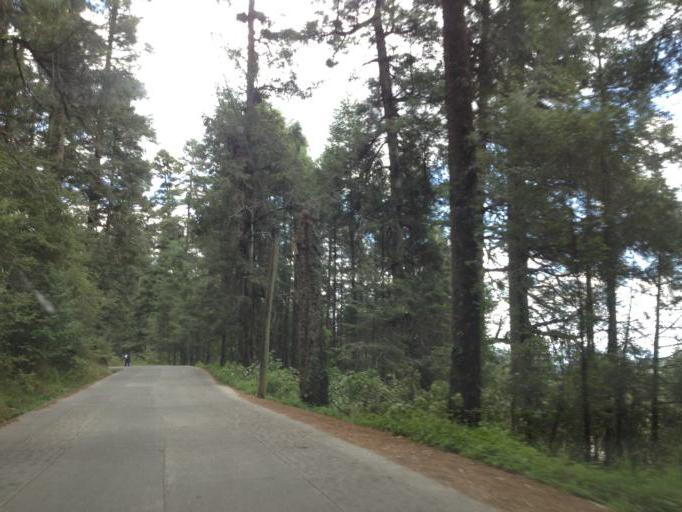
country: MX
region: Hidalgo
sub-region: Pachuca de Soto
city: San Miguel Cerezo (El Cerezo)
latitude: 20.2147
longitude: -98.7028
